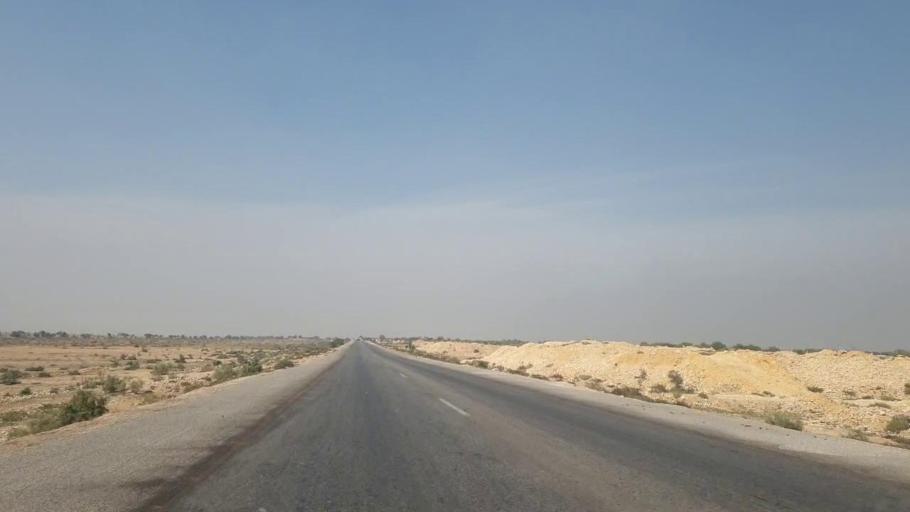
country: PK
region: Sindh
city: Hala
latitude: 25.8661
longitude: 68.2587
